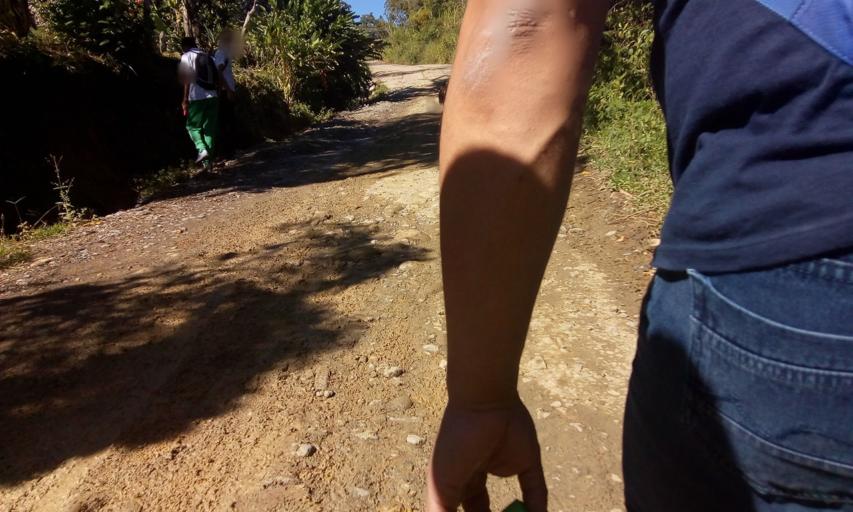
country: CO
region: Santander
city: Guepsa
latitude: 6.0027
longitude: -73.5542
